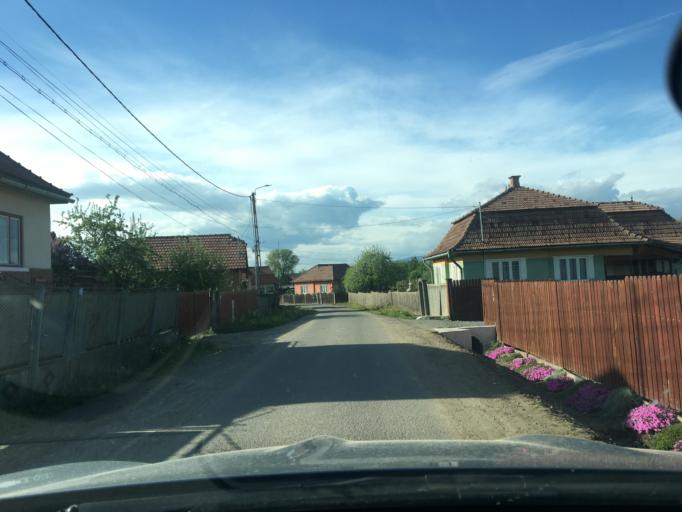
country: RO
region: Harghita
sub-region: Comuna Ditrau
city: Ditrau
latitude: 46.7954
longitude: 25.4881
